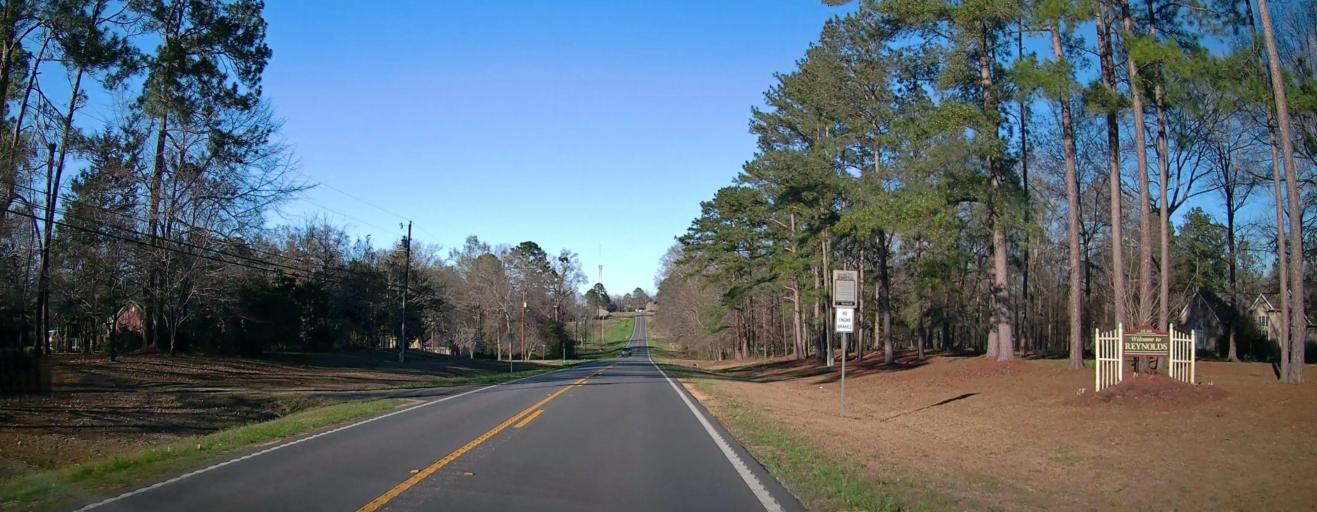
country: US
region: Georgia
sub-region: Taylor County
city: Reynolds
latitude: 32.5487
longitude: -84.0992
